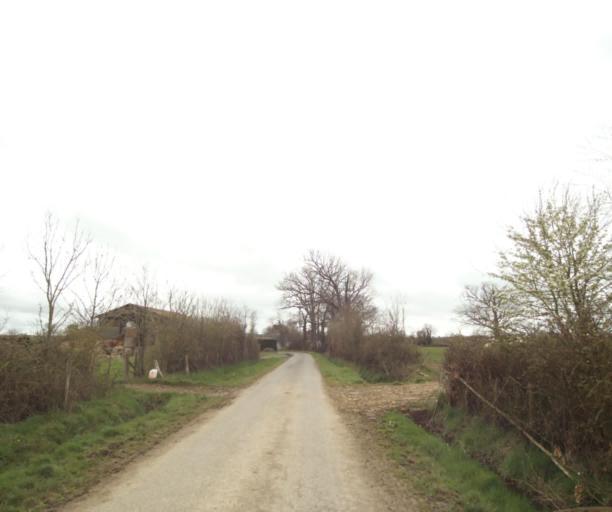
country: FR
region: Pays de la Loire
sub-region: Departement de la Loire-Atlantique
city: Bouvron
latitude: 47.4295
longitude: -1.8743
